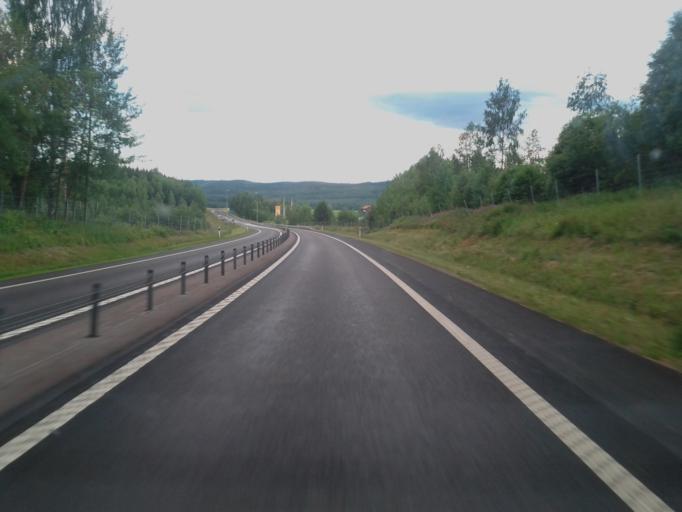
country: SE
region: Dalarna
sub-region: Borlange Kommun
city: Borlaenge
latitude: 60.4344
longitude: 15.3444
